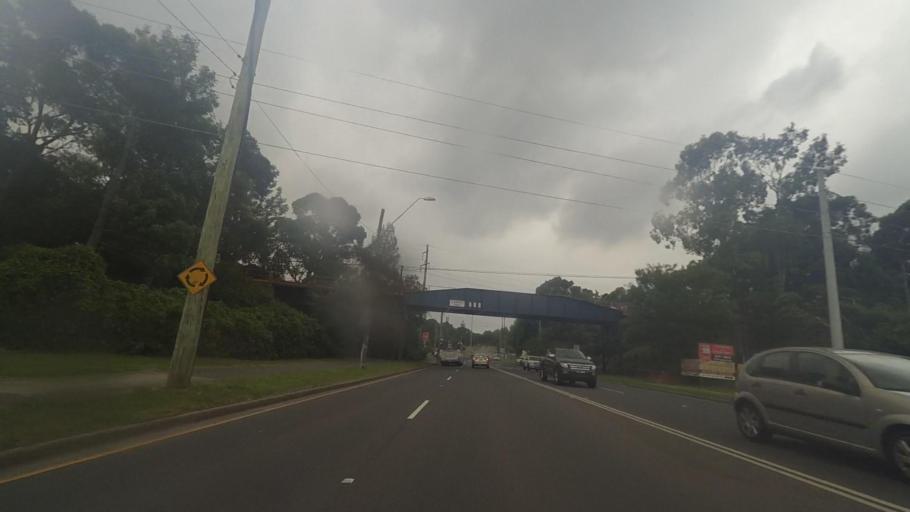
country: AU
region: New South Wales
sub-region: Wollongong
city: Cordeaux Heights
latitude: -34.4480
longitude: 150.8509
